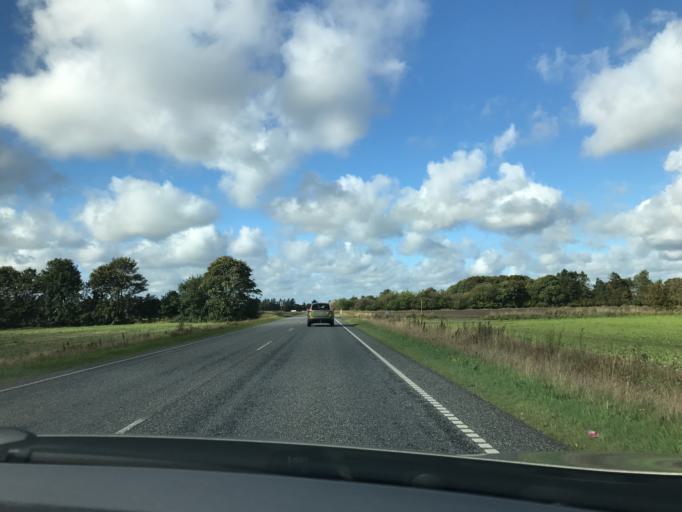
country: DK
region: South Denmark
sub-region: Billund Kommune
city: Billund
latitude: 55.7194
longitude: 9.1695
